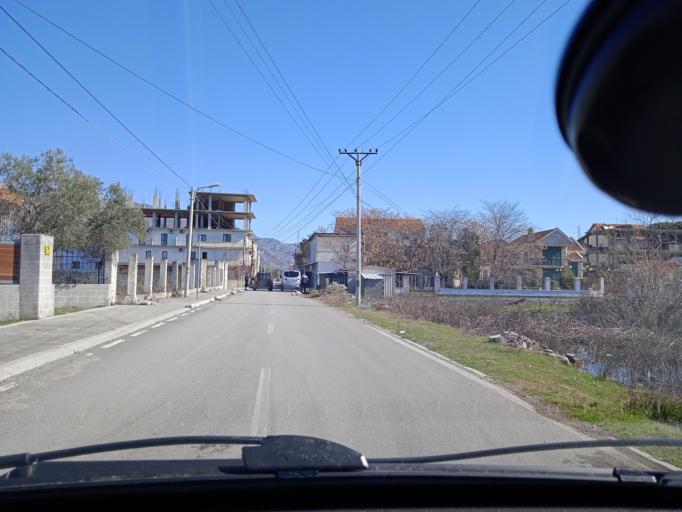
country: AL
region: Shkoder
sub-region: Rrethi i Shkodres
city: Velipoje
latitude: 41.8625
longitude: 19.4372
